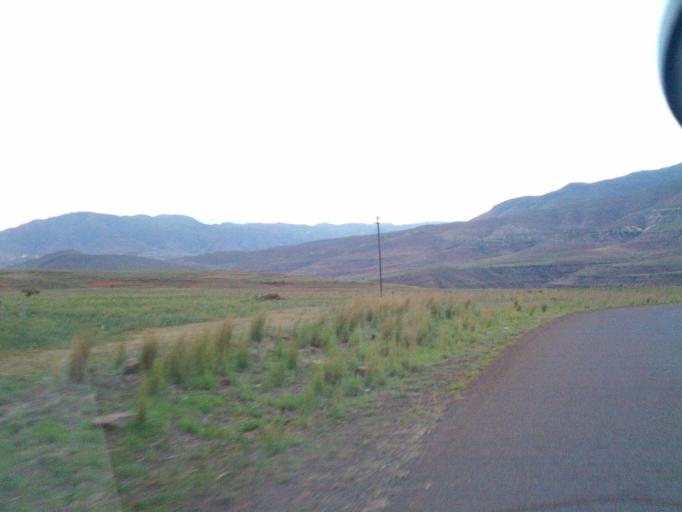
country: LS
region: Qacha's Nek
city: Qacha's Nek
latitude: -30.0589
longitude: 28.3801
